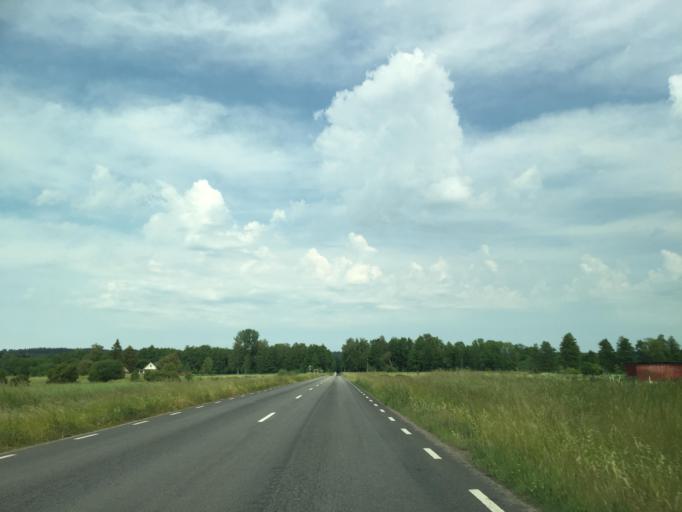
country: SE
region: Vaestra Goetaland
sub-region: Falkopings Kommun
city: Akarp
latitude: 58.3210
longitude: 13.7179
